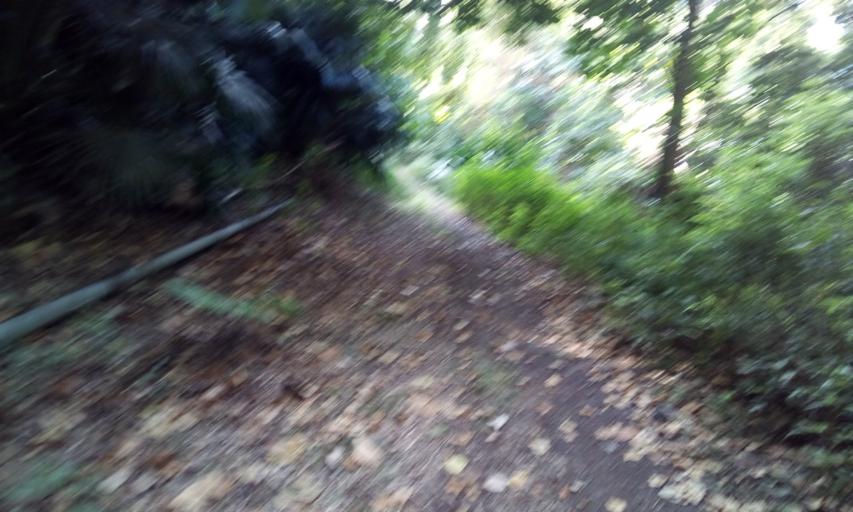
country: AU
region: New South Wales
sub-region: Wollongong
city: Cordeaux Heights
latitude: -34.4446
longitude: 150.8098
